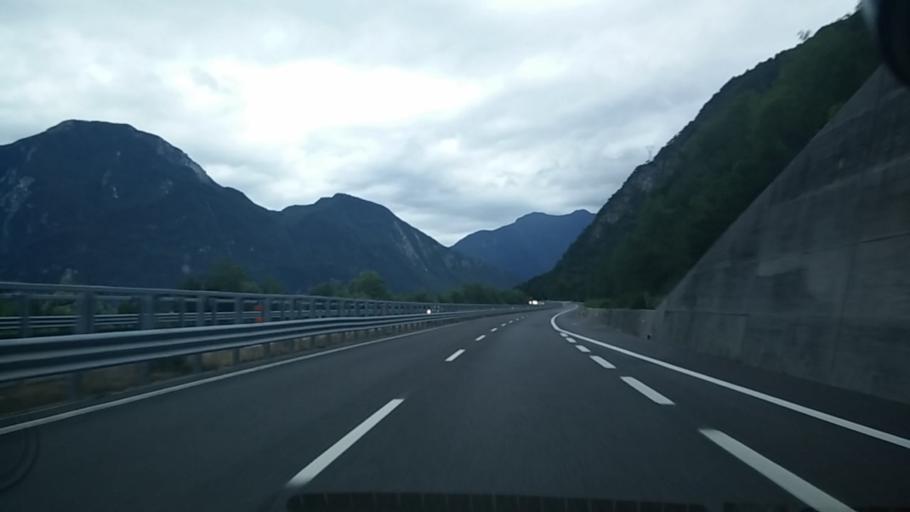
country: IT
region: Friuli Venezia Giulia
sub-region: Provincia di Udine
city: Amaro
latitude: 46.3877
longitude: 13.1285
